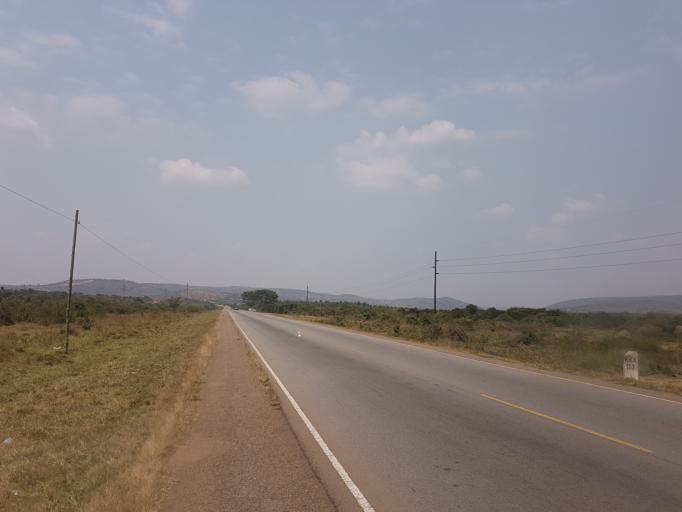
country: UG
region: Western Region
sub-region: Mbarara District
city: Mbarara
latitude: -0.5101
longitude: 30.8296
